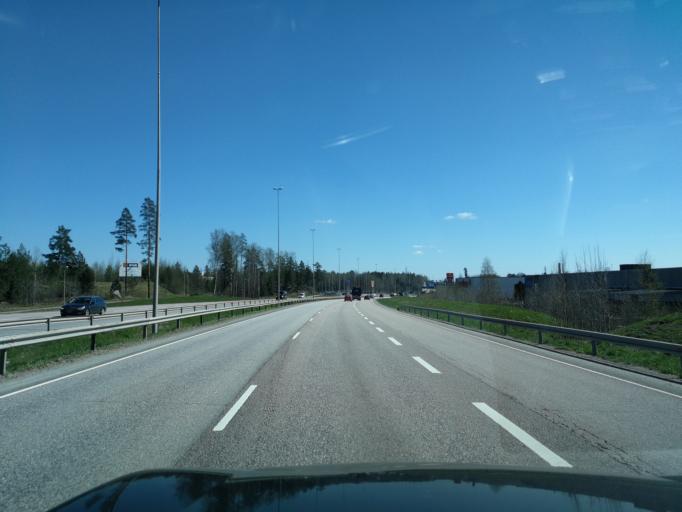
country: FI
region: Uusimaa
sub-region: Helsinki
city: Vantaa
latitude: 60.2972
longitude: 24.9244
